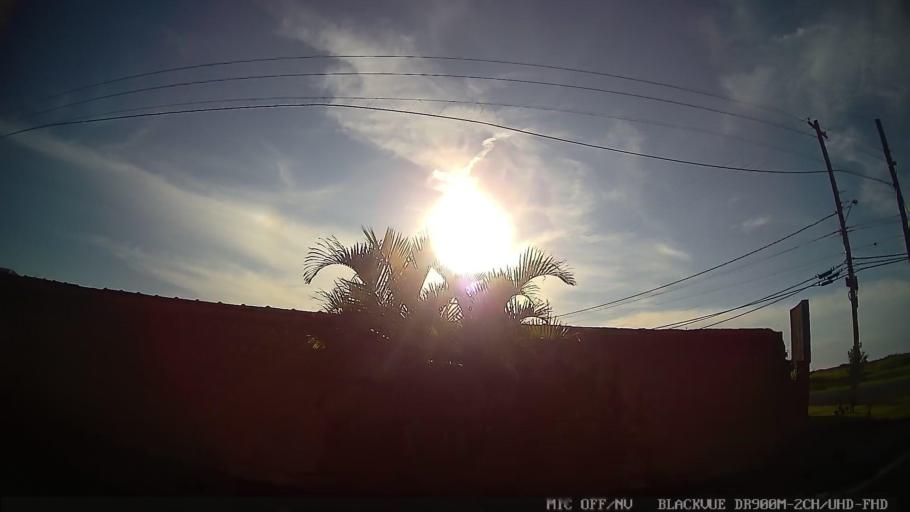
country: BR
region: Sao Paulo
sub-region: Iguape
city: Iguape
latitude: -24.7581
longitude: -47.5670
